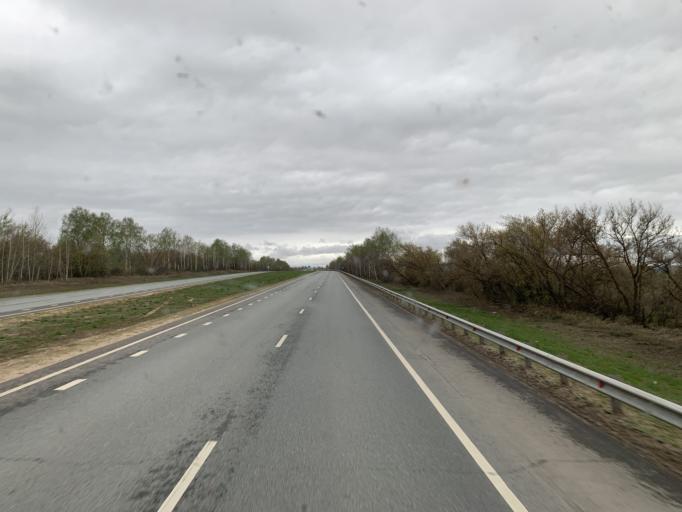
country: RU
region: Ulyanovsk
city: Kanadey
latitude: 53.1487
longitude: 47.5777
